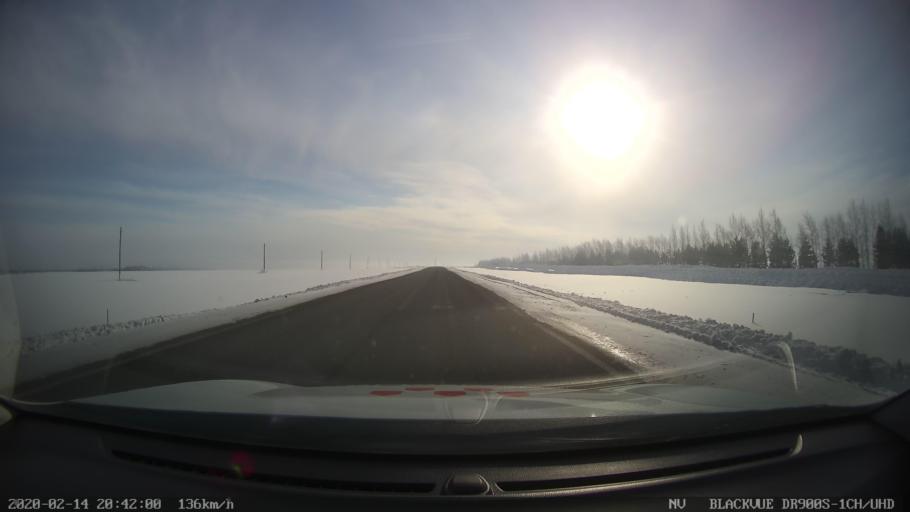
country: RU
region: Tatarstan
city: Kuybyshevskiy Zaton
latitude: 55.3224
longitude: 49.1339
